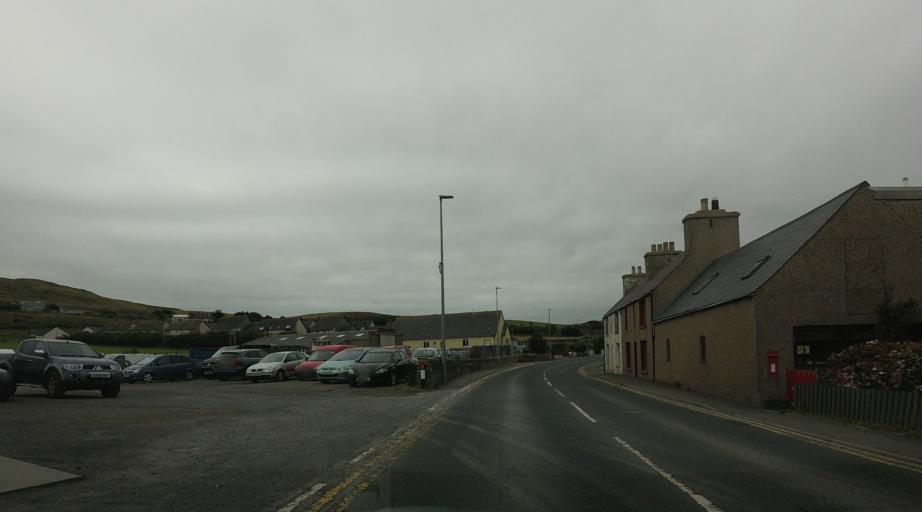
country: GB
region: Scotland
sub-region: Orkney Islands
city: Orkney
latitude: 59.0040
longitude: -3.1107
